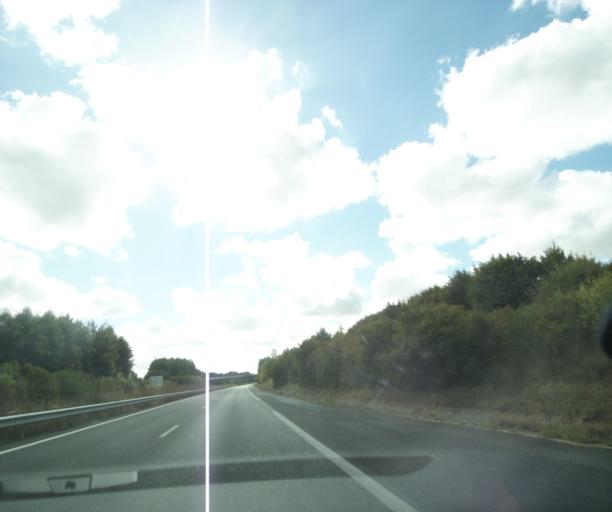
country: FR
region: Poitou-Charentes
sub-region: Departement de la Charente-Maritime
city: Cabariot
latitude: 45.9386
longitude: -0.8441
